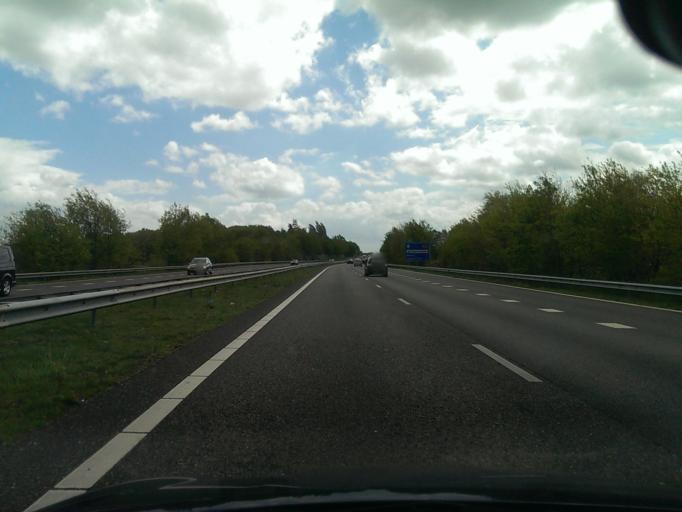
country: NL
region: North Brabant
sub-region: Gemeente Cranendonck
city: Cranendonck
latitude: 51.3180
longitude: 5.5998
